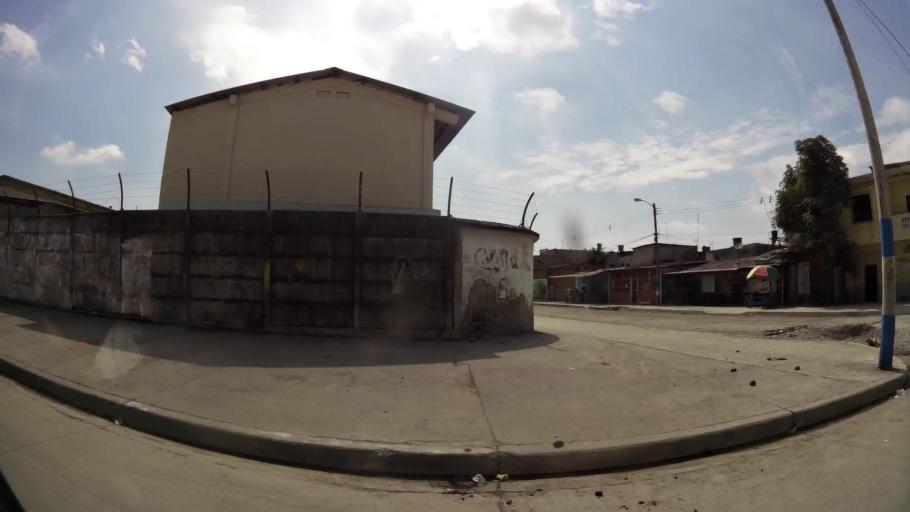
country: EC
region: Guayas
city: Guayaquil
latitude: -2.2792
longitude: -79.8839
